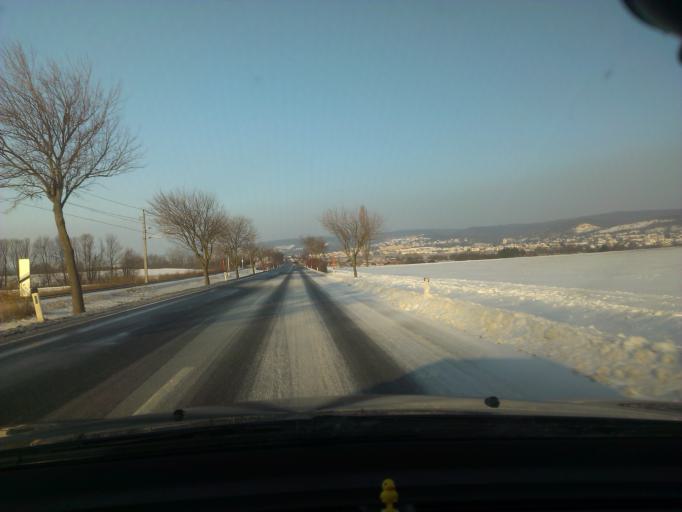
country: AT
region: Burgenland
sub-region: Eisenstadt-Umgebung
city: Trausdorf an der Wulka
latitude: 47.8435
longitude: 16.5634
